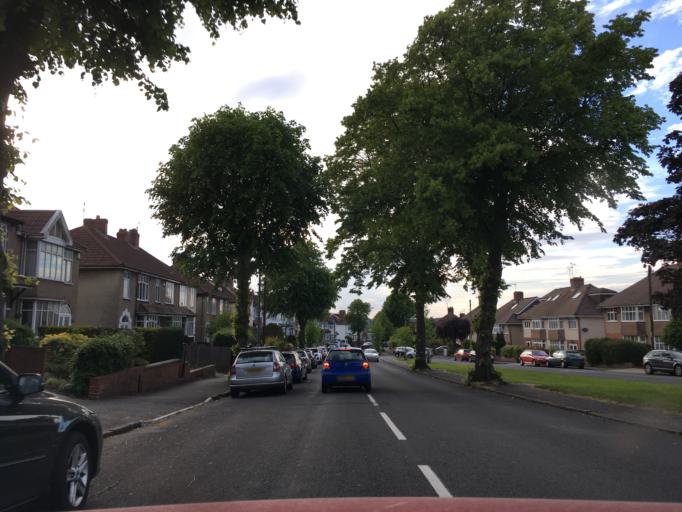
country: GB
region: England
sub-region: Bristol
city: Bristol
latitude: 51.4890
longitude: -2.5931
